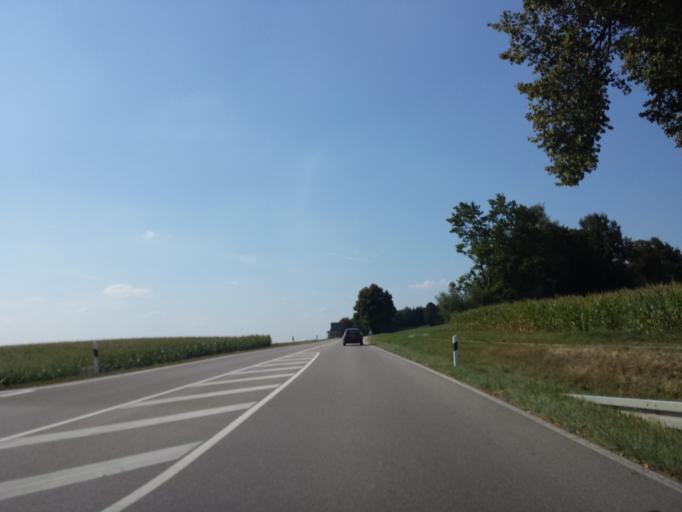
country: DE
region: Bavaria
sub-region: Swabia
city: Breitenbrunn
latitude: 48.1393
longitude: 10.4226
